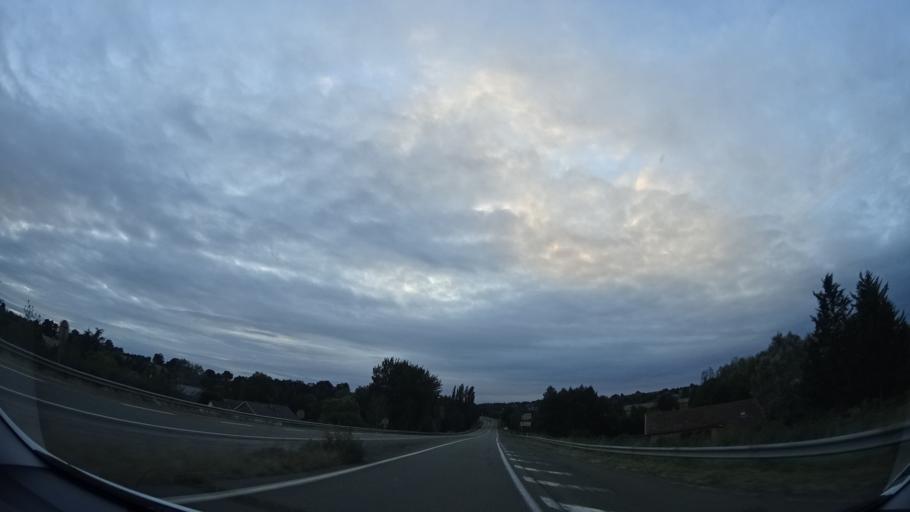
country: FR
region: Pays de la Loire
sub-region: Departement de la Mayenne
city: Sainte-Suzanne
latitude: 48.0349
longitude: -0.3845
